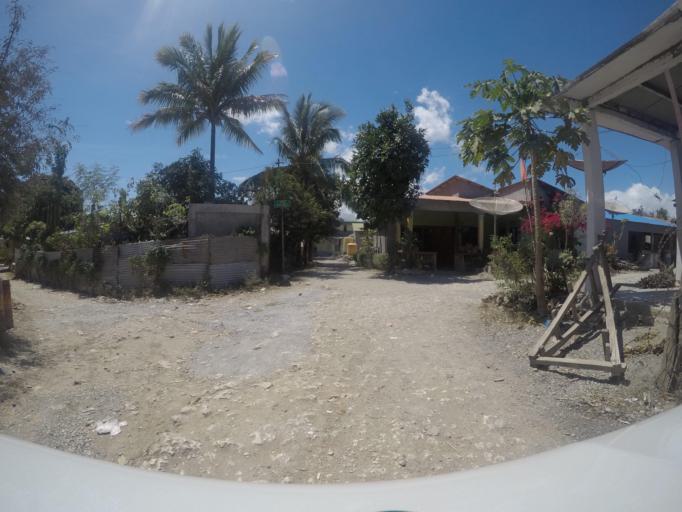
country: TL
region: Baucau
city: Baucau
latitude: -8.4824
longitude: 126.4508
